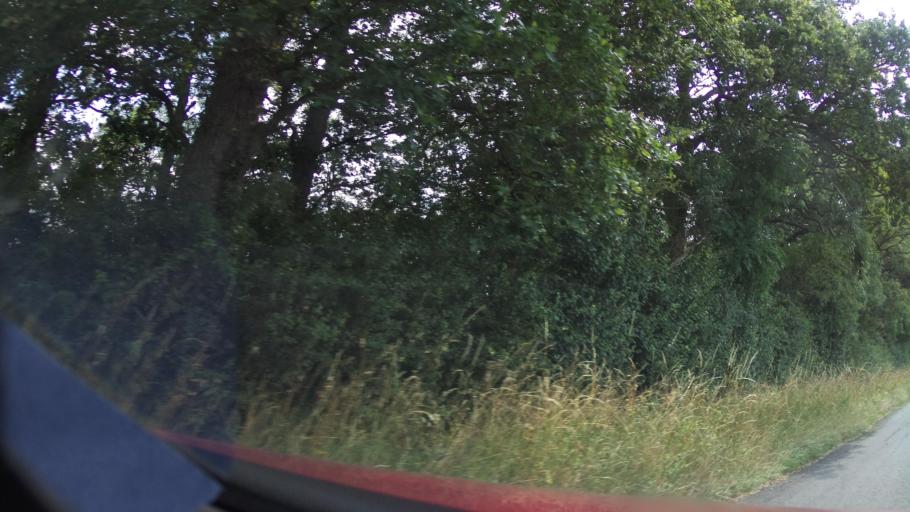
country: GB
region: England
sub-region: Wiltshire
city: Minety
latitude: 51.6102
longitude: -1.9810
